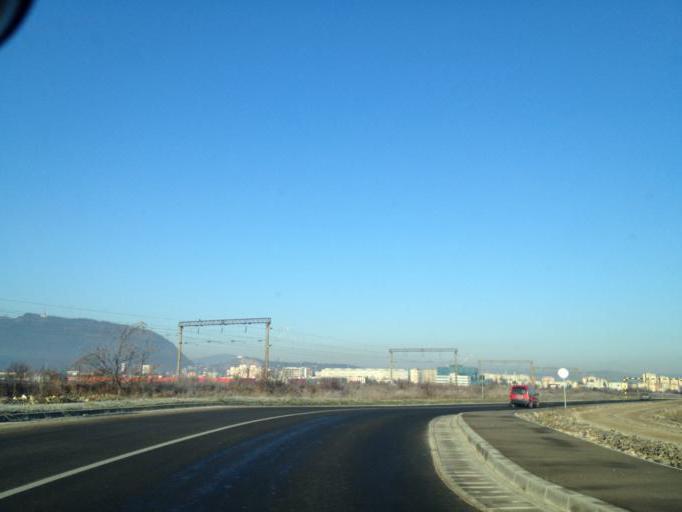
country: RO
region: Brasov
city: Brasov
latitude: 45.6285
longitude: 25.6487
